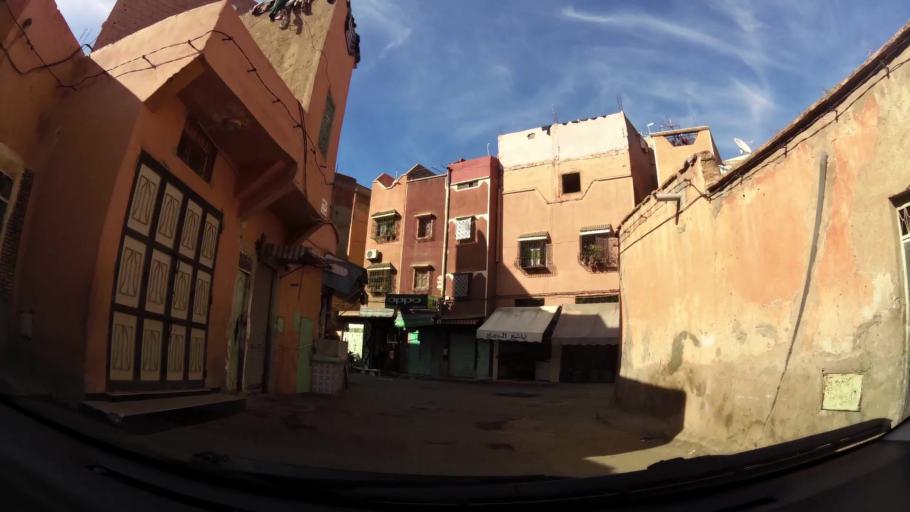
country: MA
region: Marrakech-Tensift-Al Haouz
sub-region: Marrakech
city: Marrakesh
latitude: 31.6163
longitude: -7.9665
